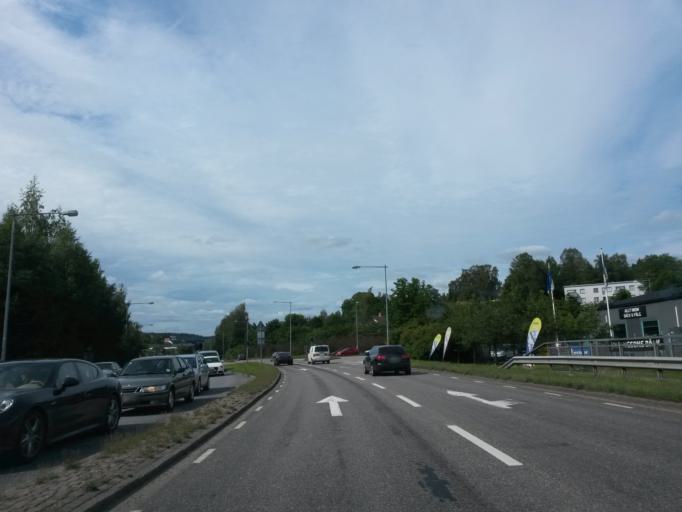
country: SE
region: Vaestra Goetaland
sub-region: Boras Kommun
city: Boras
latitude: 57.7079
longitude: 12.9497
